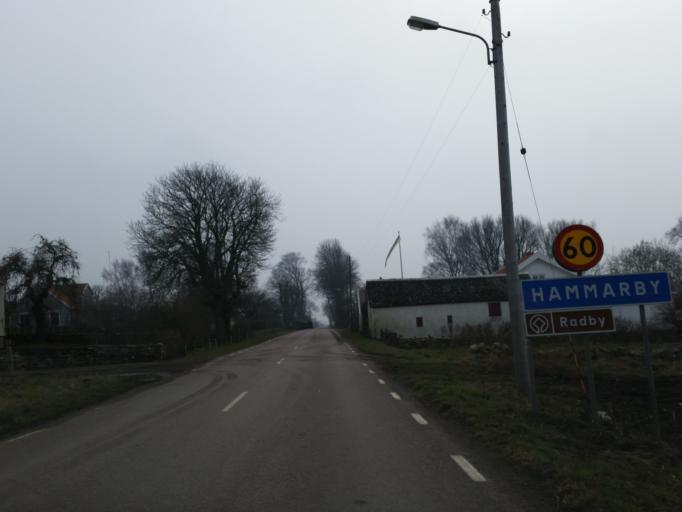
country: SE
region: Kalmar
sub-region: Morbylanga Kommun
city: Moerbylanga
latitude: 56.3924
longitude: 16.4134
